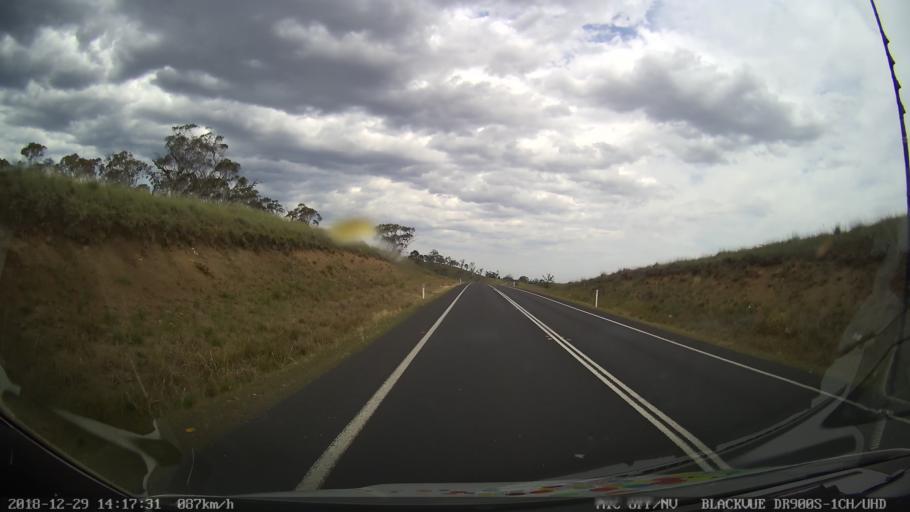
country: AU
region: New South Wales
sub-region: Cooma-Monaro
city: Cooma
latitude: -36.4798
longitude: 149.2590
